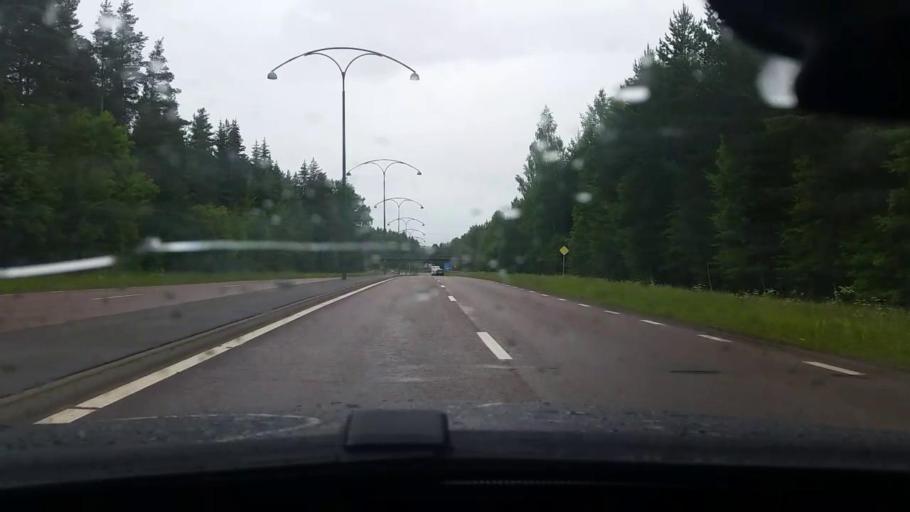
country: SE
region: Dalarna
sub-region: Borlange Kommun
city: Borlaenge
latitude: 60.5026
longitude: 15.3908
